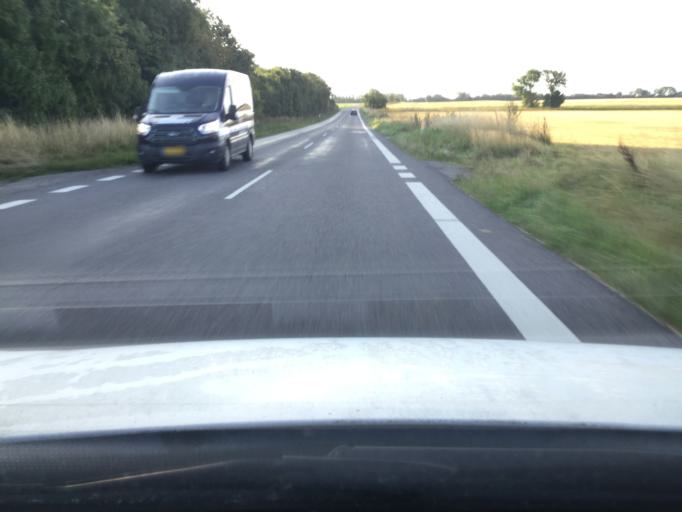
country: DK
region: Zealand
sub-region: Lolland Kommune
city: Rodby
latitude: 54.7884
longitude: 11.2856
